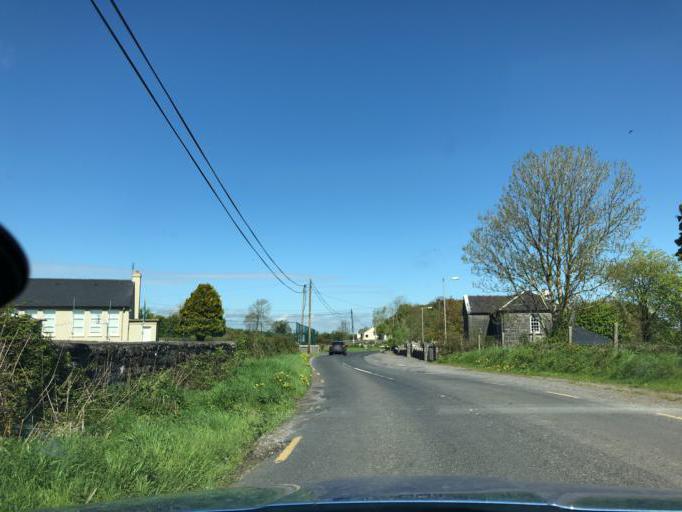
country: IE
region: Connaught
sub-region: County Galway
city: Portumna
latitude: 53.1382
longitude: -8.3657
